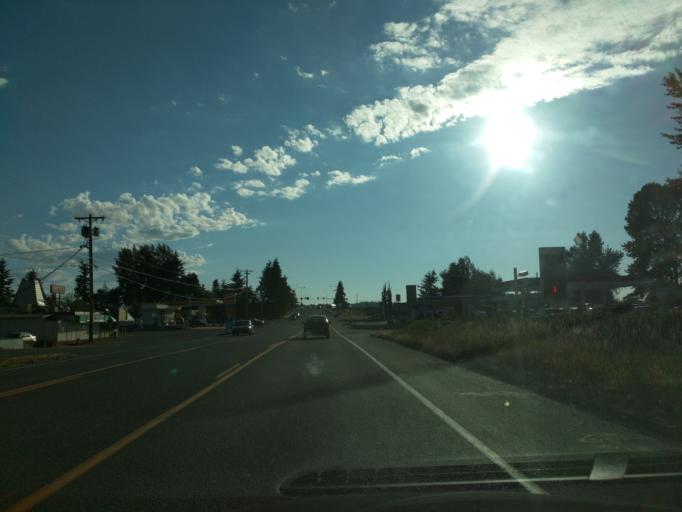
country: US
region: Washington
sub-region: Snohomish County
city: Smokey Point
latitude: 48.1881
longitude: -122.1977
